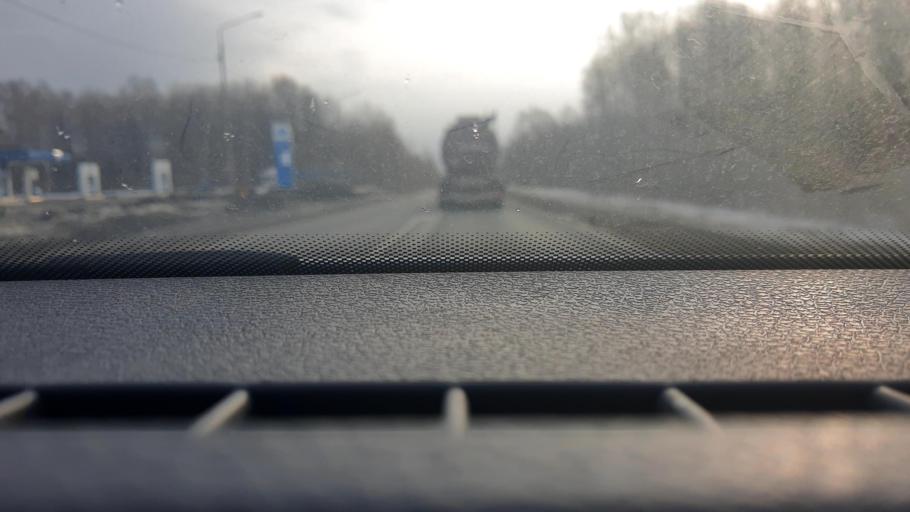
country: RU
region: Chelyabinsk
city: Asha
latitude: 54.8826
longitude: 57.2605
